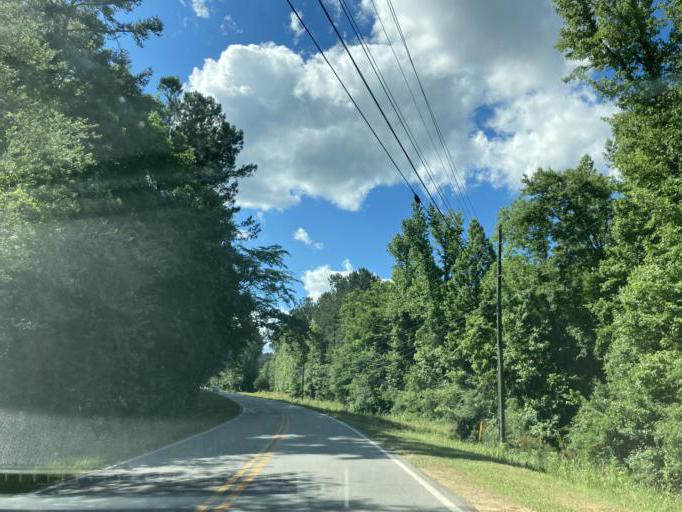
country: US
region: Georgia
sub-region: Jones County
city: Gray
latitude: 32.9942
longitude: -83.5506
